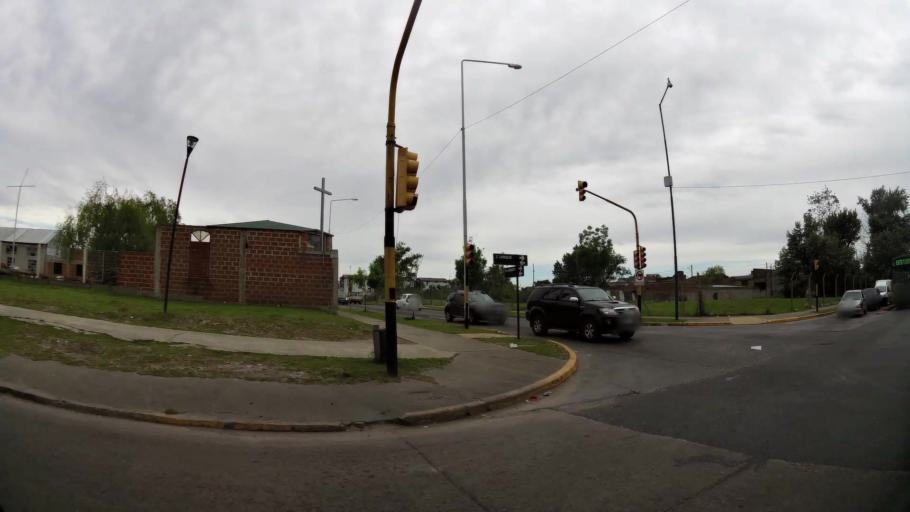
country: AR
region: Buenos Aires
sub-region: Partido de Avellaneda
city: Avellaneda
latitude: -34.6840
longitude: -58.3622
